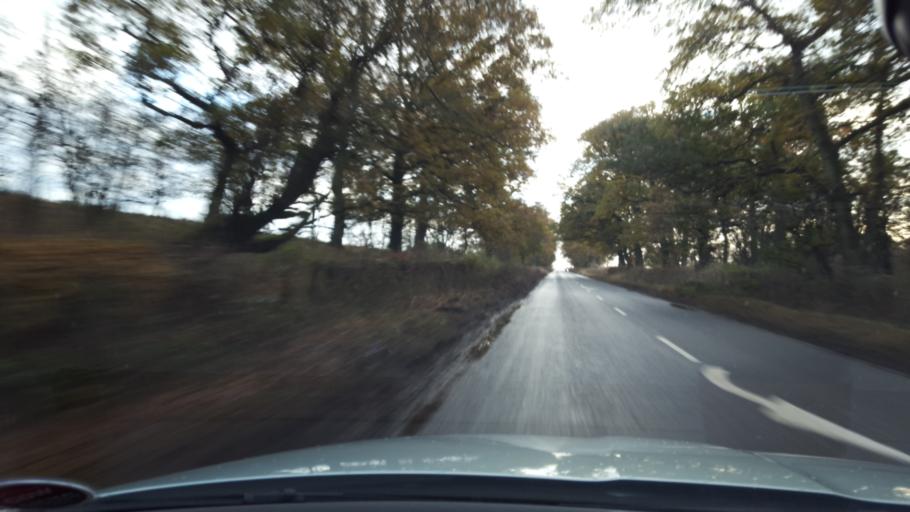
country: GB
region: Scotland
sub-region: Perth and Kinross
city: Milnathort
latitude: 56.2560
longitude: -3.3742
